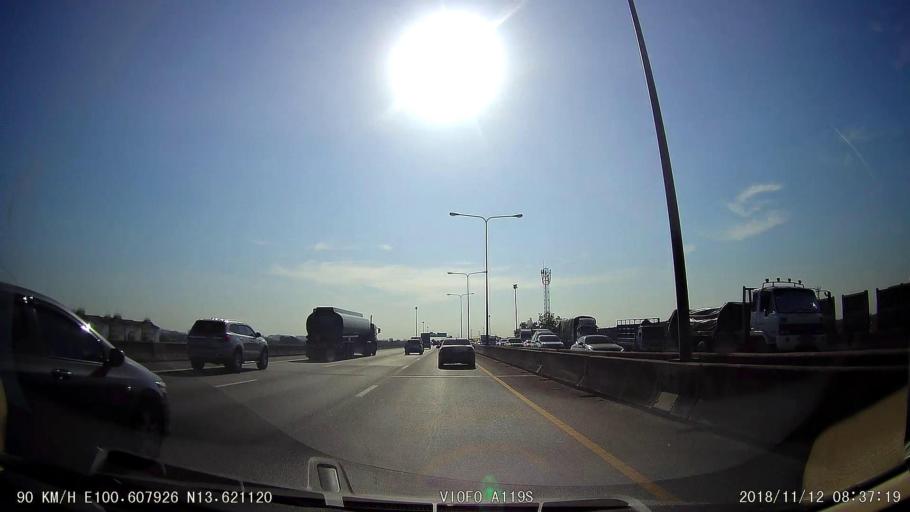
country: TH
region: Samut Prakan
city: Samut Prakan
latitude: 13.6206
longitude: 100.6089
